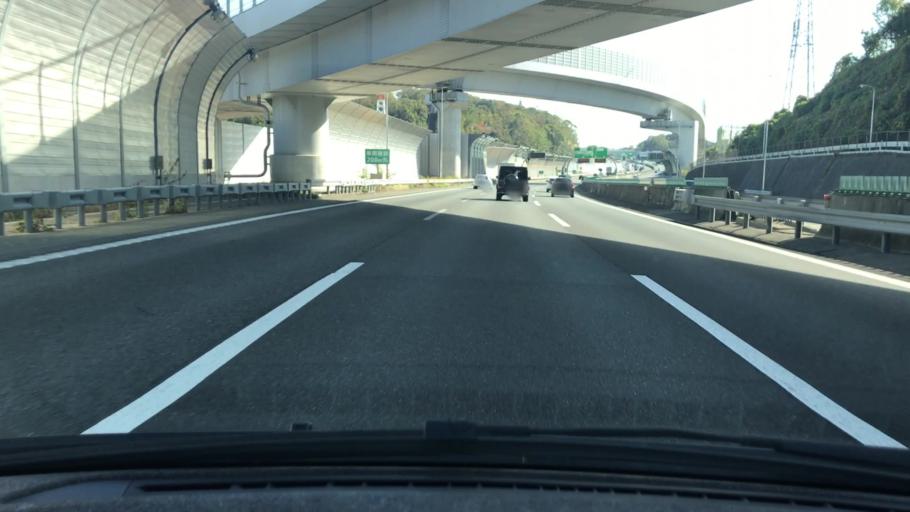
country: JP
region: Osaka
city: Takatsuki
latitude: 34.8672
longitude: 135.6255
